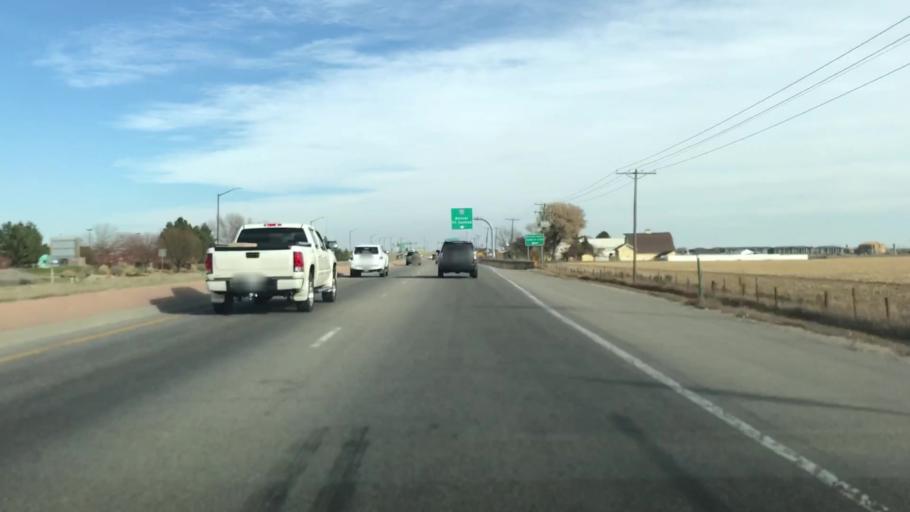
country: US
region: Colorado
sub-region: Larimer County
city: Loveland
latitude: 40.4070
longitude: -105.0017
